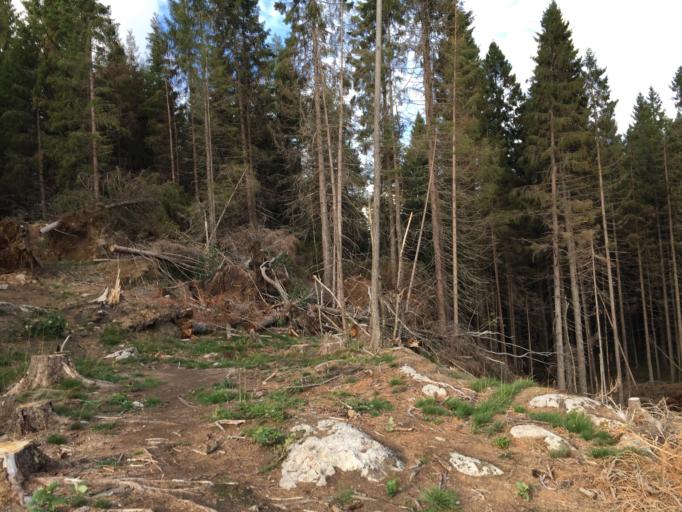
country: NO
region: Akershus
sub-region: Raelingen
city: Fjerdingby
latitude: 59.9220
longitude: 11.0321
